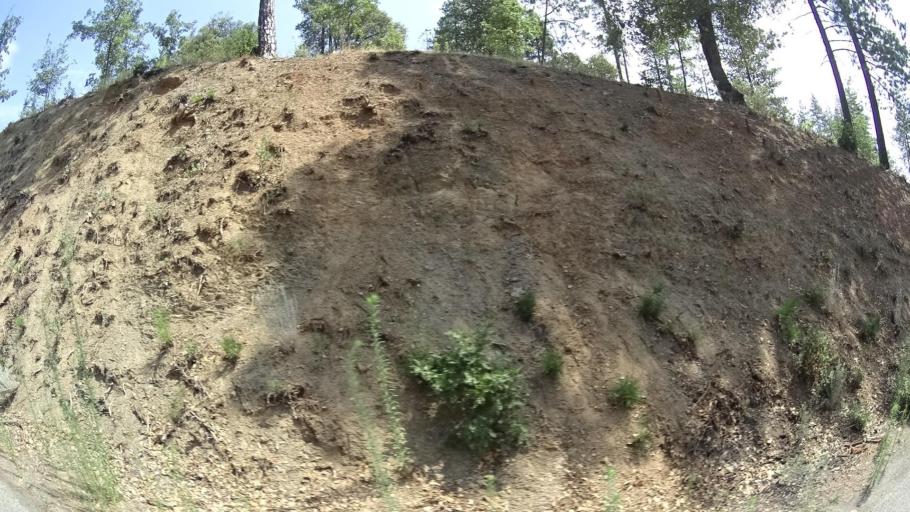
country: US
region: California
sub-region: Mariposa County
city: Midpines
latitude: 37.7254
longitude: -120.1070
